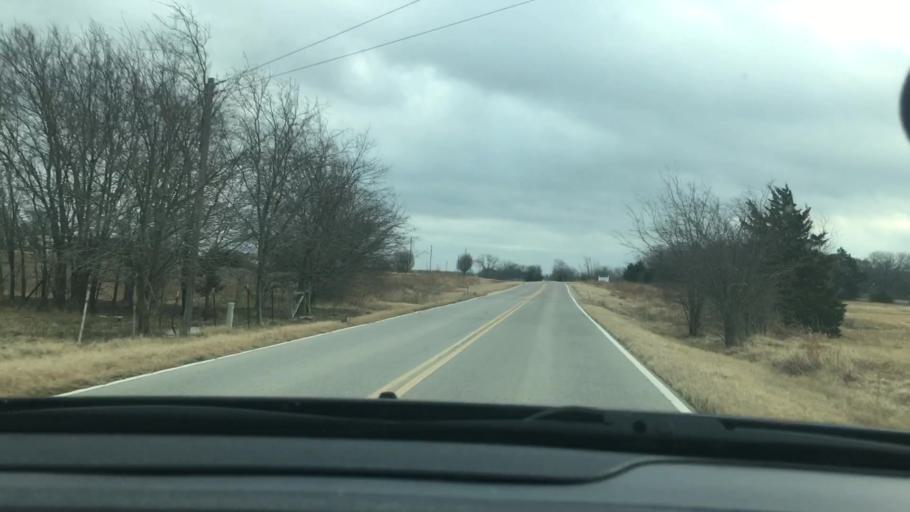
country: US
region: Oklahoma
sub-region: Bryan County
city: Durant
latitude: 34.0847
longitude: -96.4106
